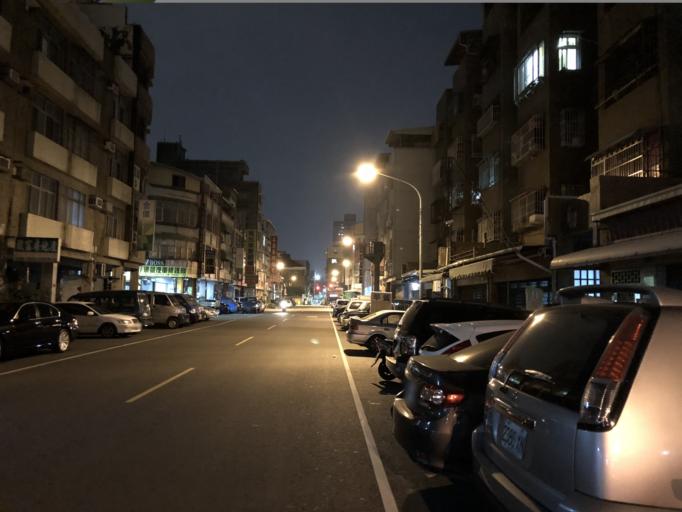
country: TW
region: Kaohsiung
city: Kaohsiung
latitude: 22.6375
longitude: 120.3313
